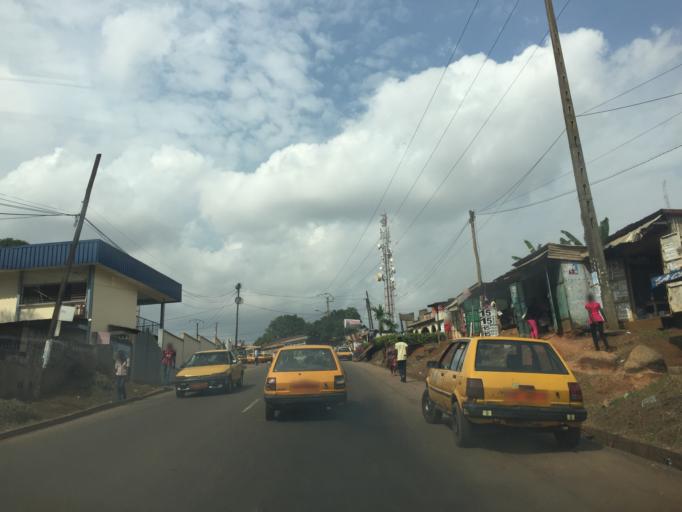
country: CM
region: Centre
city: Yaounde
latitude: 3.8554
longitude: 11.5023
